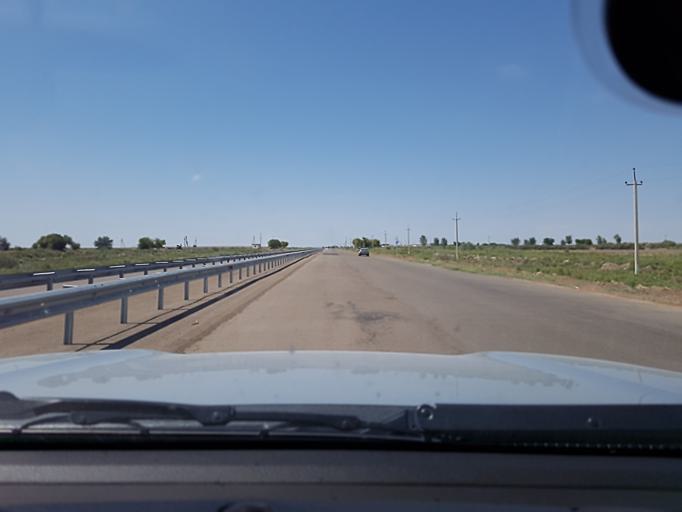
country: TM
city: Akdepe
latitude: 41.7404
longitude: 59.2421
